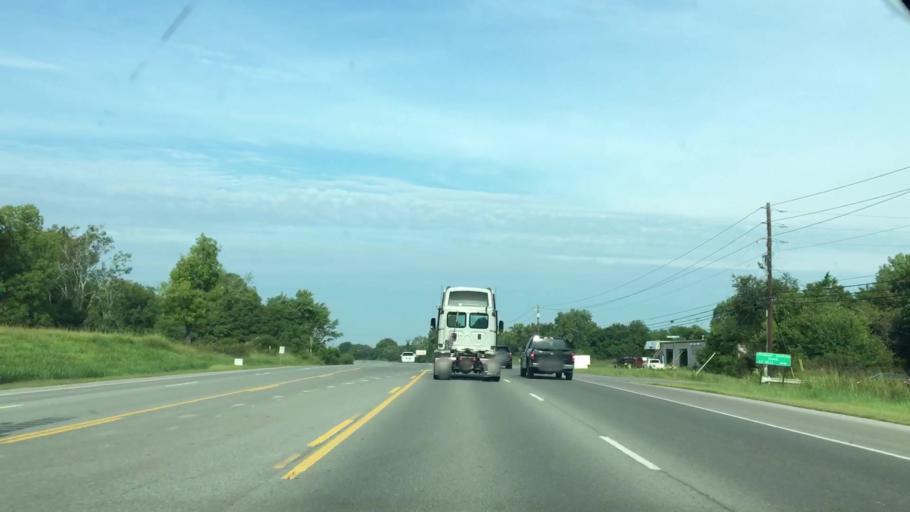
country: US
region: Tennessee
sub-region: Wilson County
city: Lebanon
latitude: 36.2386
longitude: -86.4003
